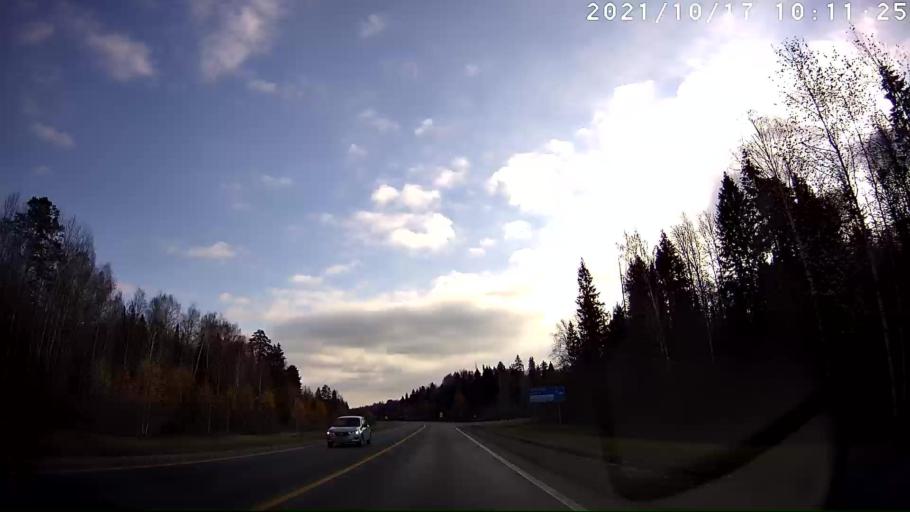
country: RU
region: Mariy-El
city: Sovetskiy
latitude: 56.7386
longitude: 48.3918
